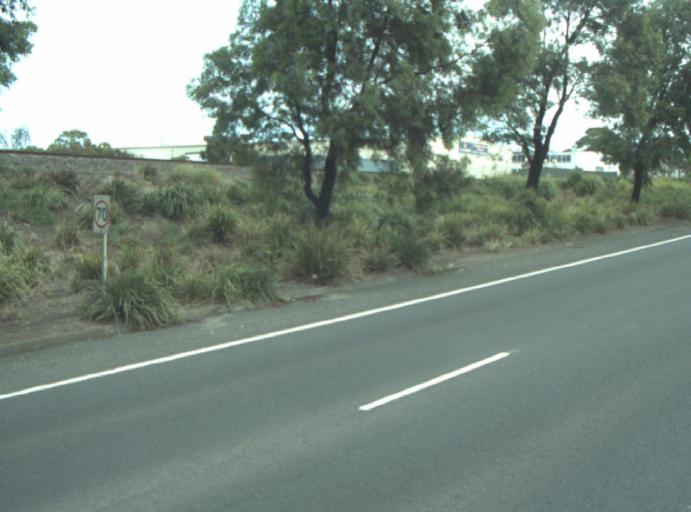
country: AU
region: Victoria
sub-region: Greater Geelong
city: Geelong West
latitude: -38.1267
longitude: 144.3519
